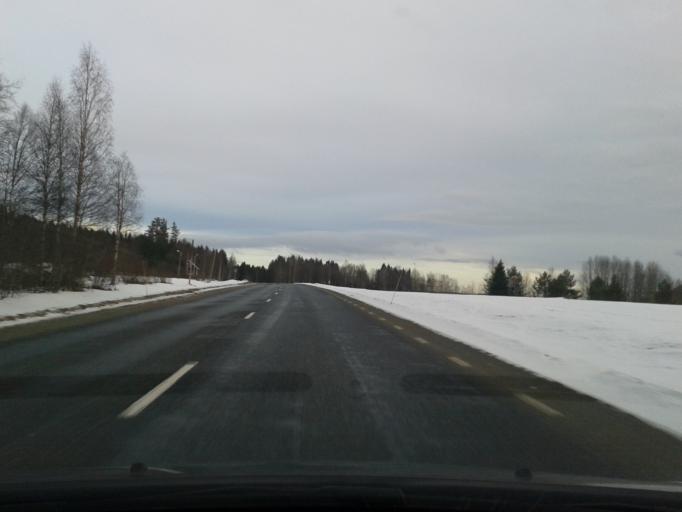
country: SE
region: Vaesternorrland
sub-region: Solleftea Kommun
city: As
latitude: 63.4447
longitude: 16.9125
